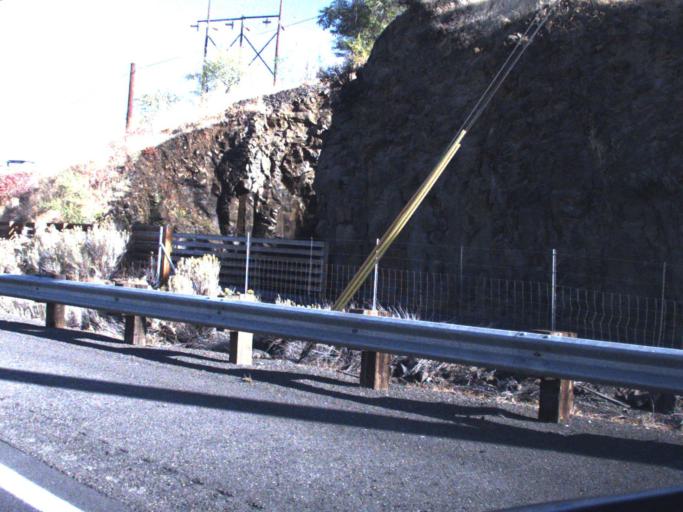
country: US
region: Washington
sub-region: Yakima County
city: Gleed
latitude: 46.6956
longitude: -120.6534
